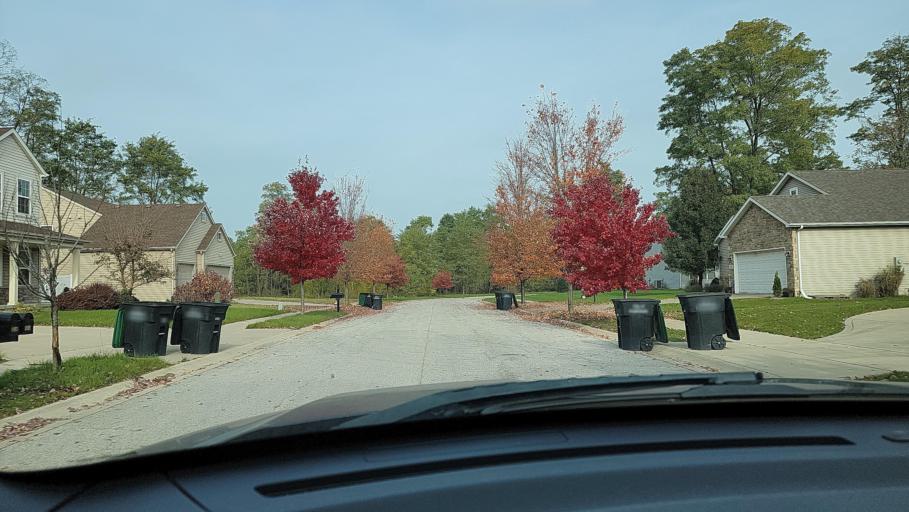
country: US
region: Indiana
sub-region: Porter County
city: Portage
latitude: 41.5965
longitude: -87.1706
